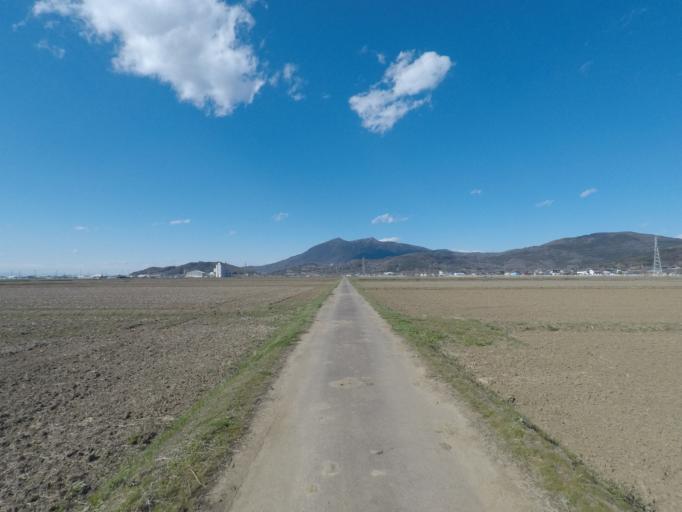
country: JP
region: Ibaraki
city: Tsukuba
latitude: 36.1591
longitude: 140.1015
